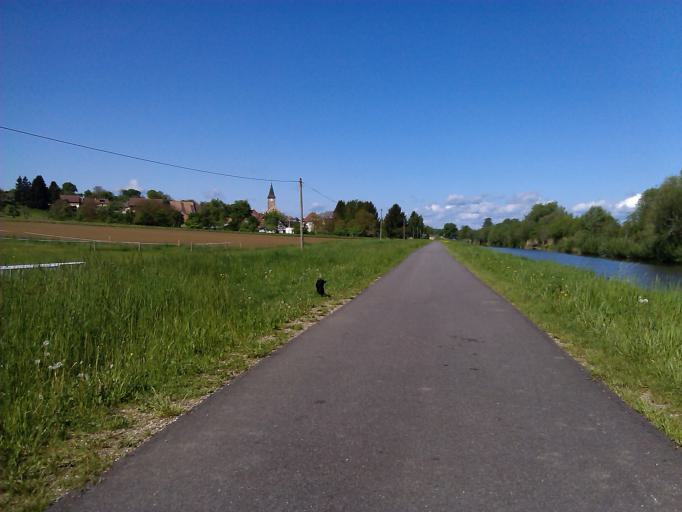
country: FR
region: Alsace
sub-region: Departement du Haut-Rhin
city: Aspach
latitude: 47.6659
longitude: 7.1898
